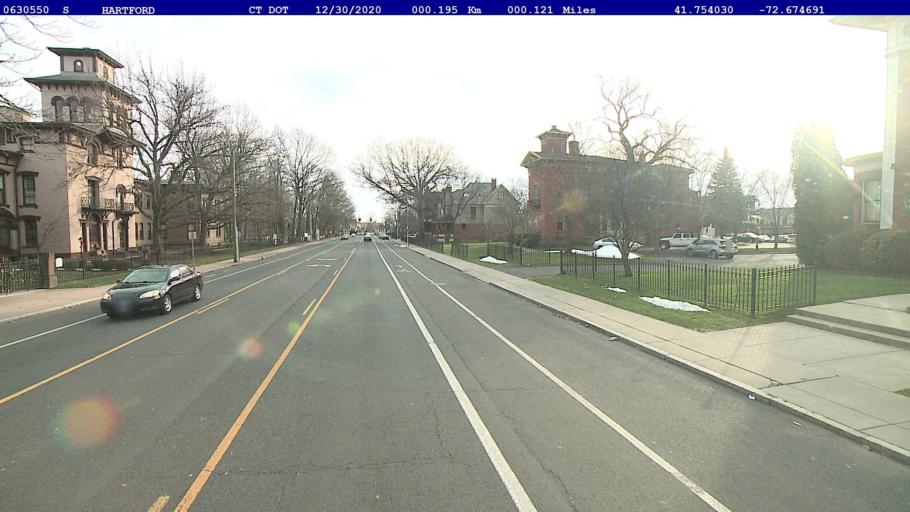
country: US
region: Connecticut
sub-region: Hartford County
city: Hartford
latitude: 41.7540
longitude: -72.6747
